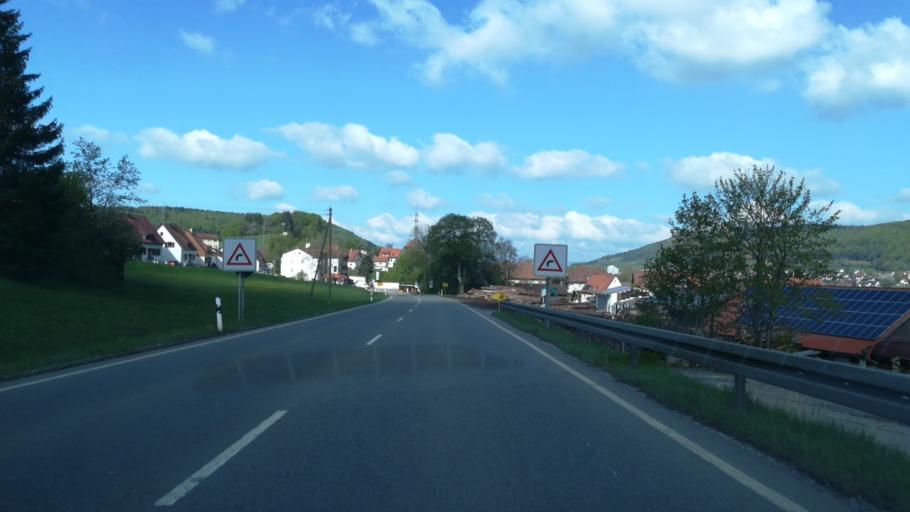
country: DE
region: Baden-Wuerttemberg
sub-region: Freiburg Region
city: Blumberg
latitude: 47.8356
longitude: 8.5599
